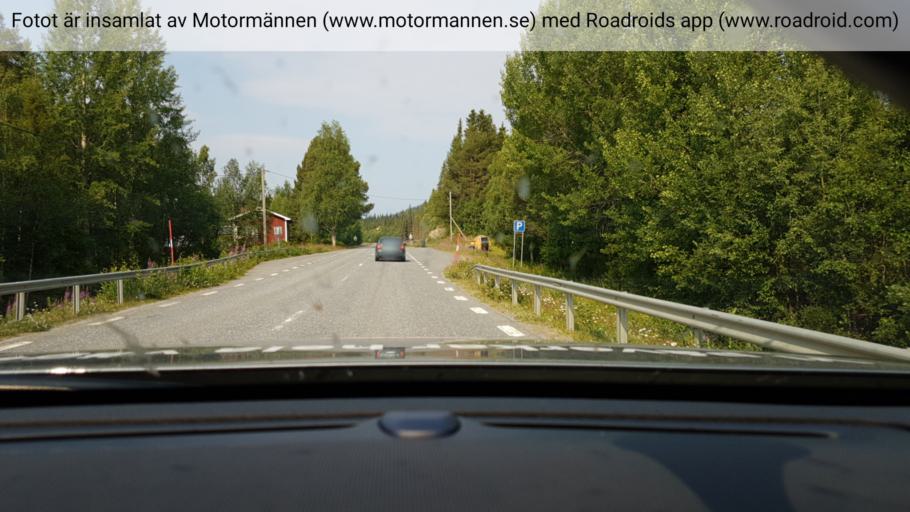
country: SE
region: Vaesterbotten
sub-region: Vilhelmina Kommun
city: Sjoberg
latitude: 65.4726
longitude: 16.0438
